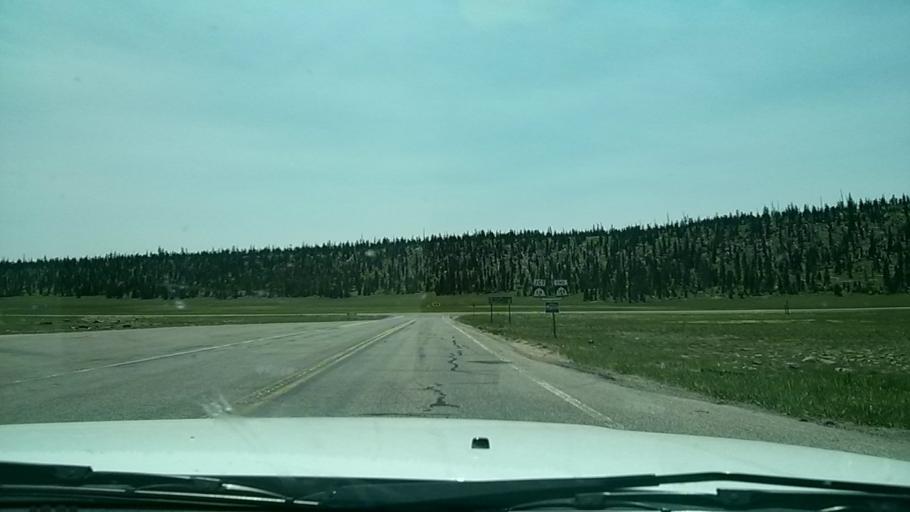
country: US
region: Utah
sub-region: Iron County
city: Cedar City
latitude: 37.5740
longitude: -112.8373
